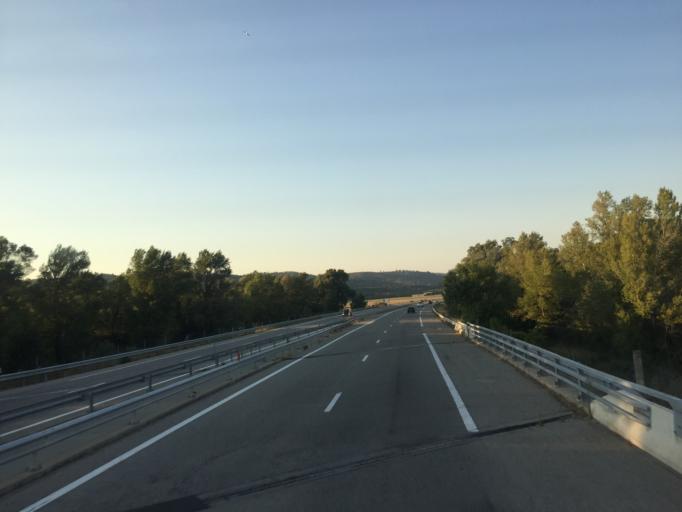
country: FR
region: Provence-Alpes-Cote d'Azur
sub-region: Departement du Vaucluse
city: Beaumont-de-Pertuis
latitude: 43.7190
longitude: 5.7368
